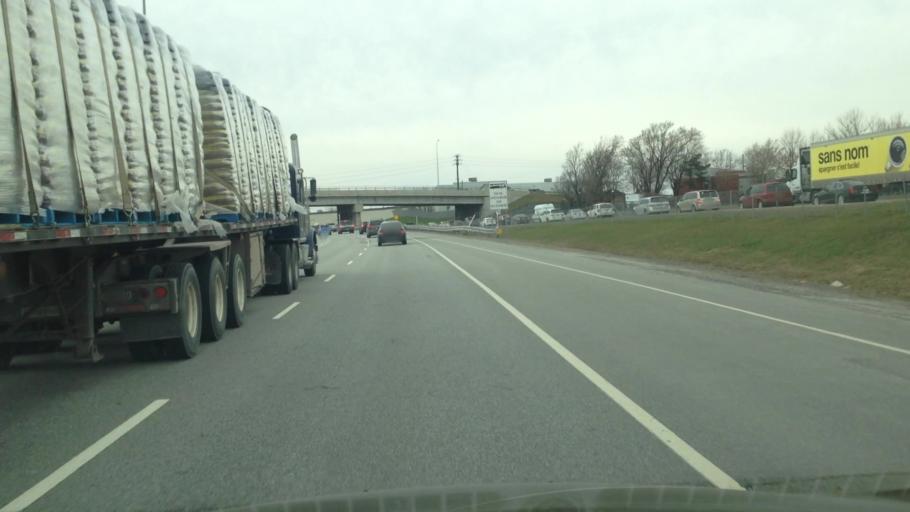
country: CA
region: Quebec
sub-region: Laval
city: Laval
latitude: 45.5787
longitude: -73.7536
